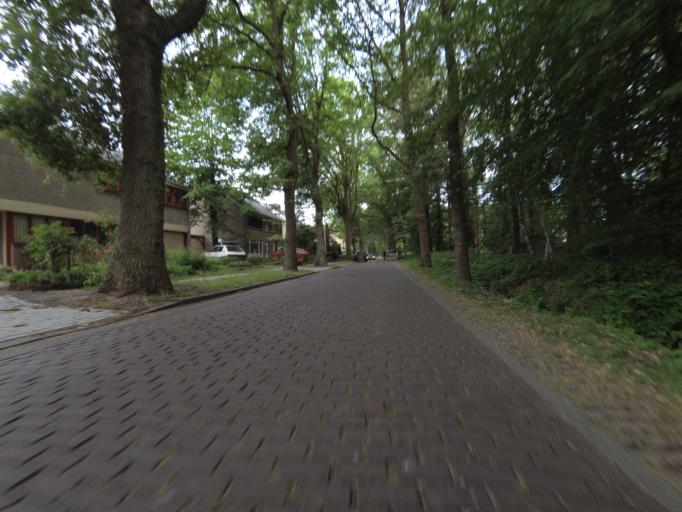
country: NL
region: Overijssel
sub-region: Gemeente Hengelo
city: Hengelo
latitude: 52.2059
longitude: 6.7973
